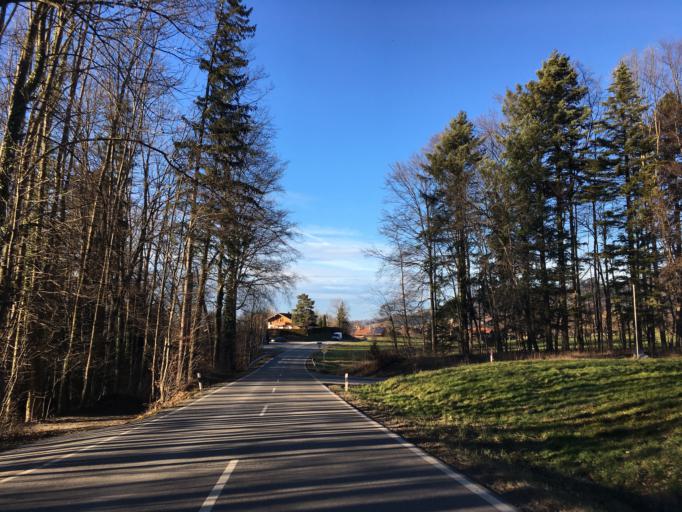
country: DE
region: Bavaria
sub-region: Upper Bavaria
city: Nussdorf am Inn
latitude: 47.7277
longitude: 12.1629
